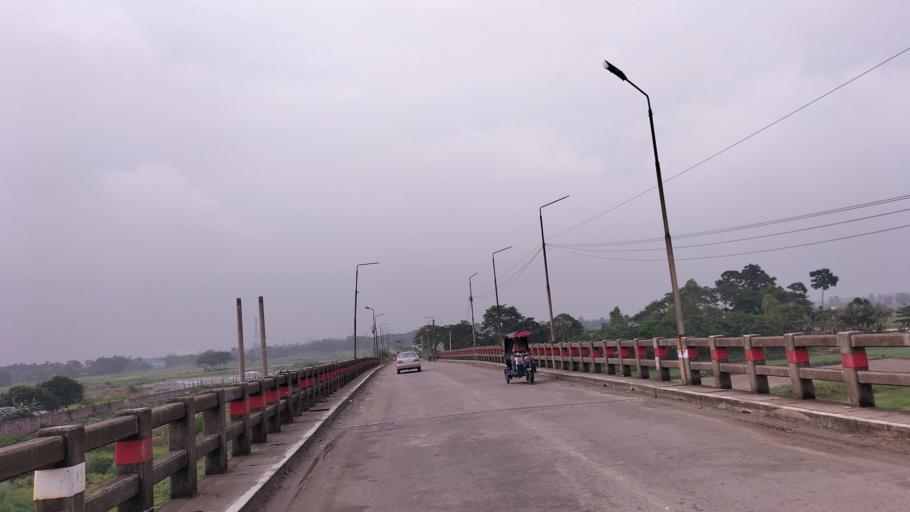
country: BD
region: Dhaka
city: Azimpur
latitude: 23.7545
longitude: 90.2496
